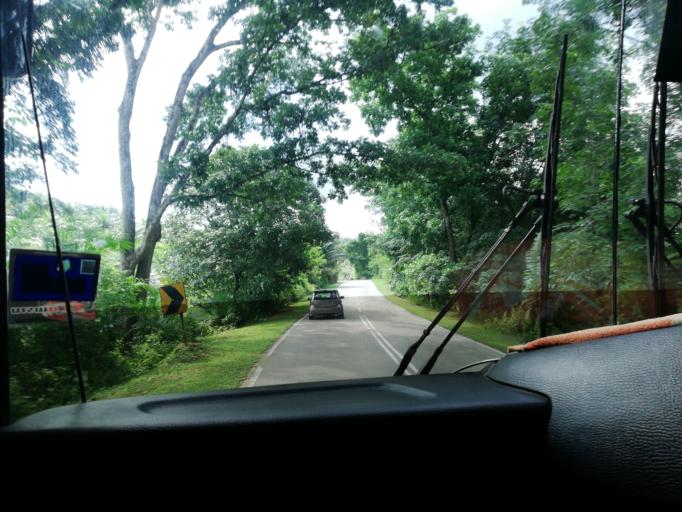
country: MY
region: Kedah
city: Kulim
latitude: 5.3200
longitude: 100.5958
